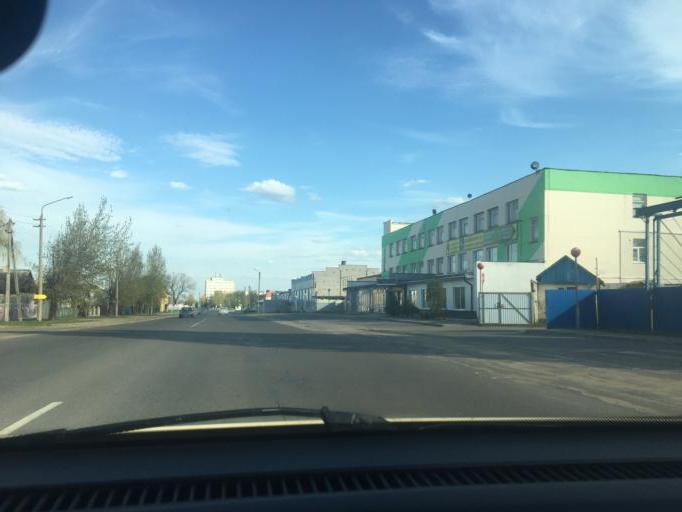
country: BY
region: Mogilev
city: Babruysk
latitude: 53.1539
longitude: 29.1806
